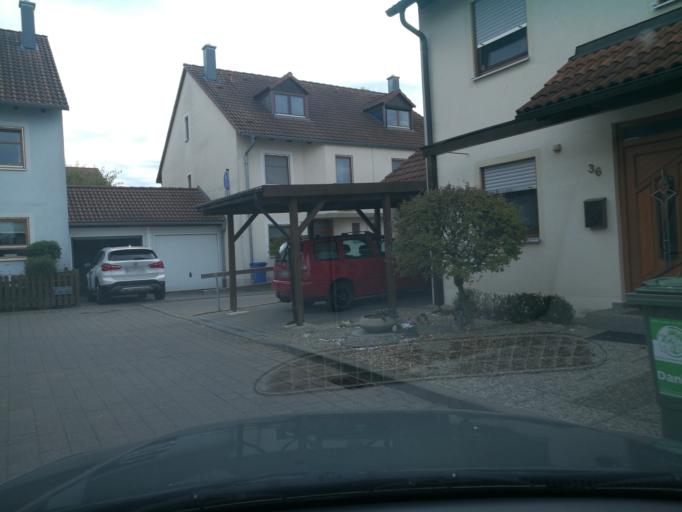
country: DE
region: Bavaria
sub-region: Regierungsbezirk Mittelfranken
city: Furth
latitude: 49.4864
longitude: 10.9683
